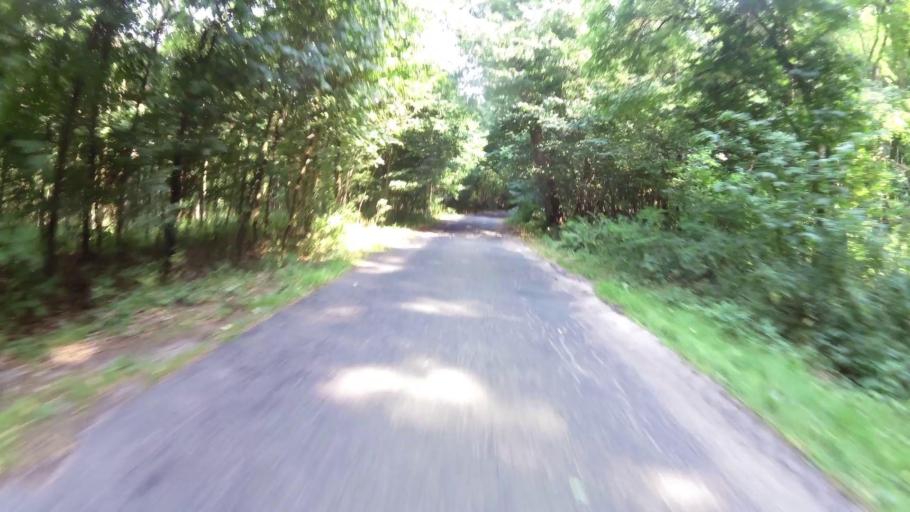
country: PL
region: West Pomeranian Voivodeship
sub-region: Powiat gryfinski
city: Mieszkowice
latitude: 52.8531
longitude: 14.5215
